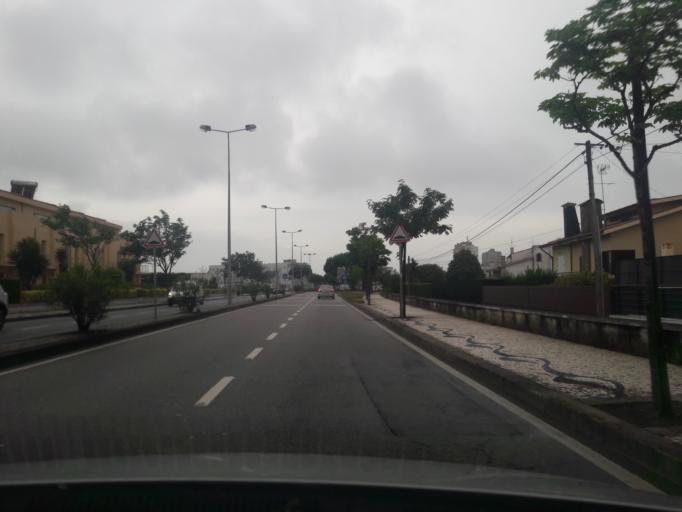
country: PT
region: Porto
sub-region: Povoa de Varzim
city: Povoa de Varzim
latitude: 41.3909
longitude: -8.7605
